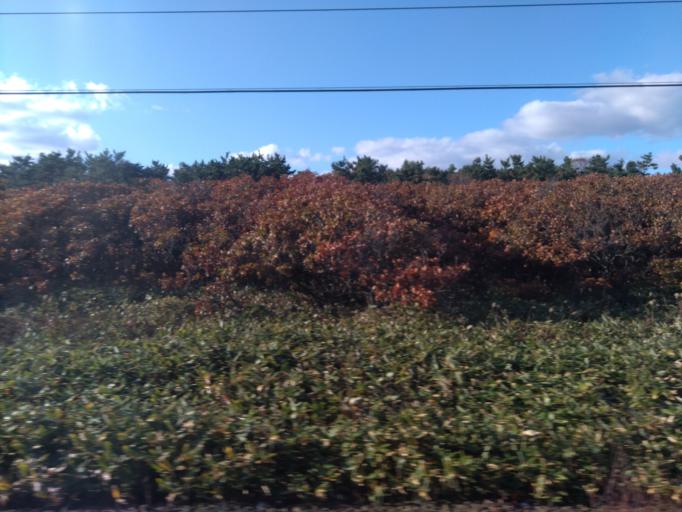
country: JP
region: Hokkaido
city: Niseko Town
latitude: 42.5552
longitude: 140.4233
